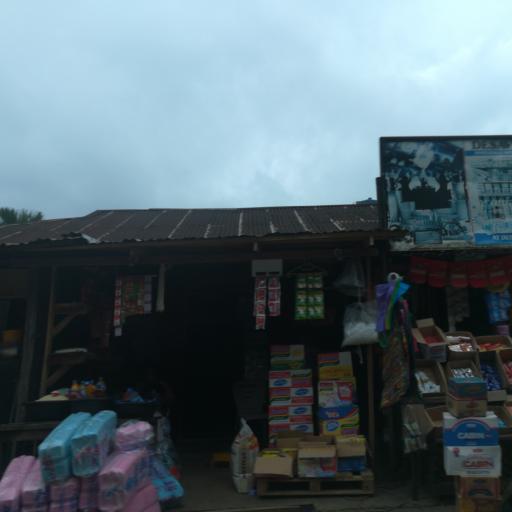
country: NG
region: Rivers
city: Port Harcourt
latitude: 4.8105
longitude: 7.0479
